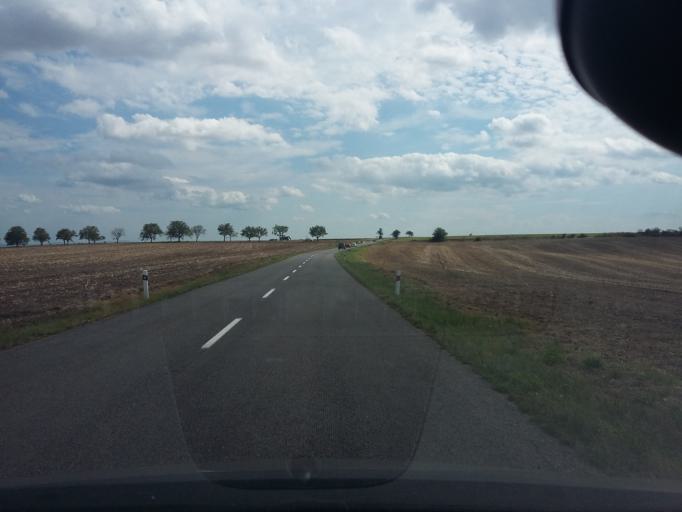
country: SK
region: Trnavsky
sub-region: Okres Skalica
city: Holic
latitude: 48.7619
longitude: 17.1729
